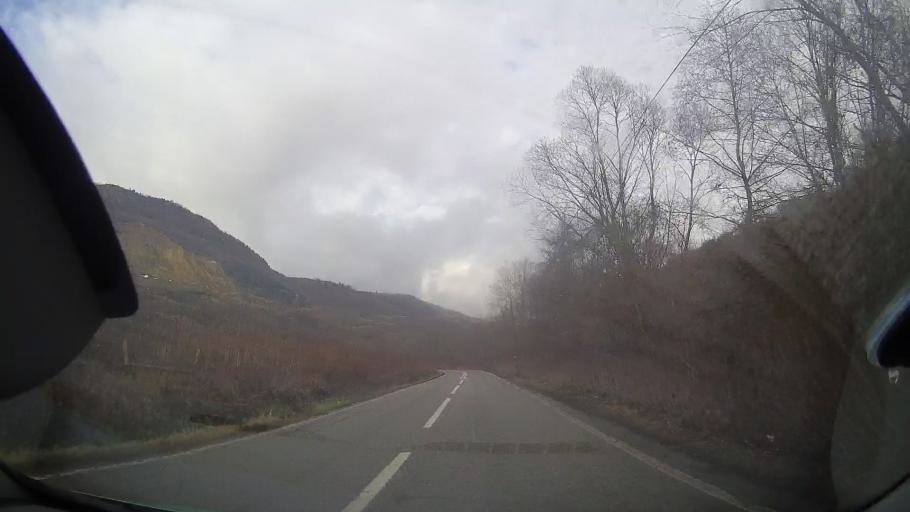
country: RO
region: Alba
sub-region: Comuna Ocolis
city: Ocolis
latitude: 46.4498
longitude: 23.4693
